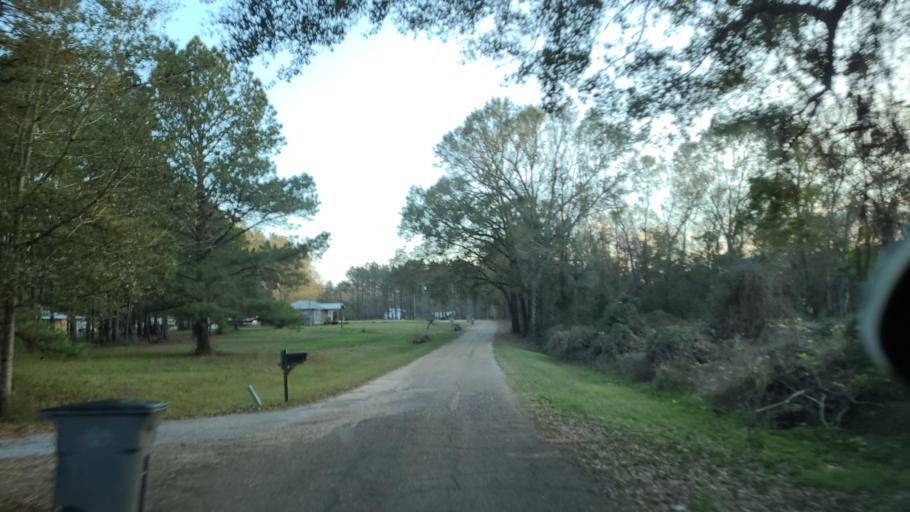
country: US
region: Mississippi
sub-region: Forrest County
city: Hattiesburg
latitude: 31.1799
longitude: -89.2200
